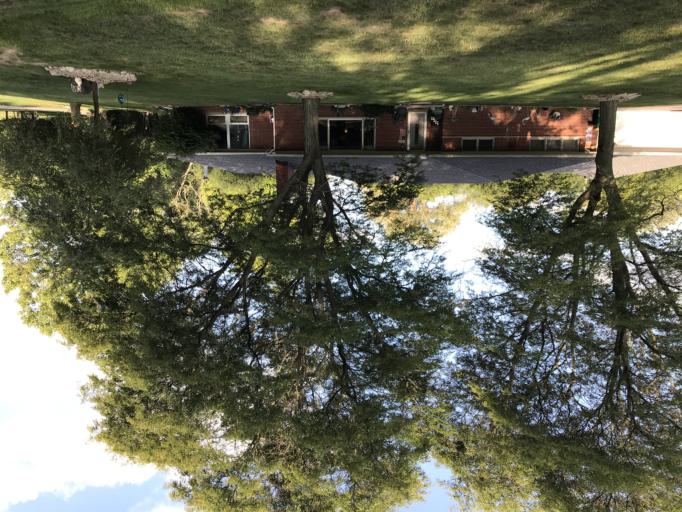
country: US
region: Michigan
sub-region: Oakland County
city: Farmington Hills
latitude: 42.4818
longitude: -83.3495
